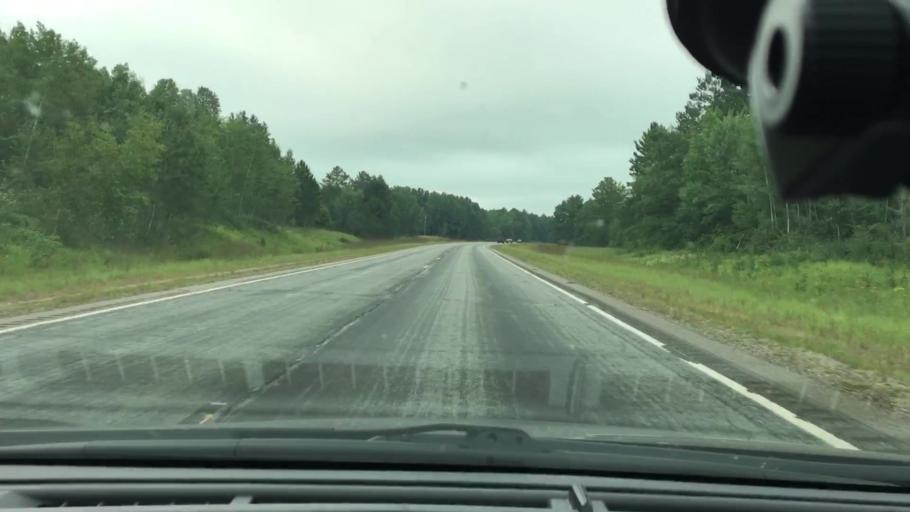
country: US
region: Minnesota
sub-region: Crow Wing County
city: Cross Lake
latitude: 46.6728
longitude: -93.9520
